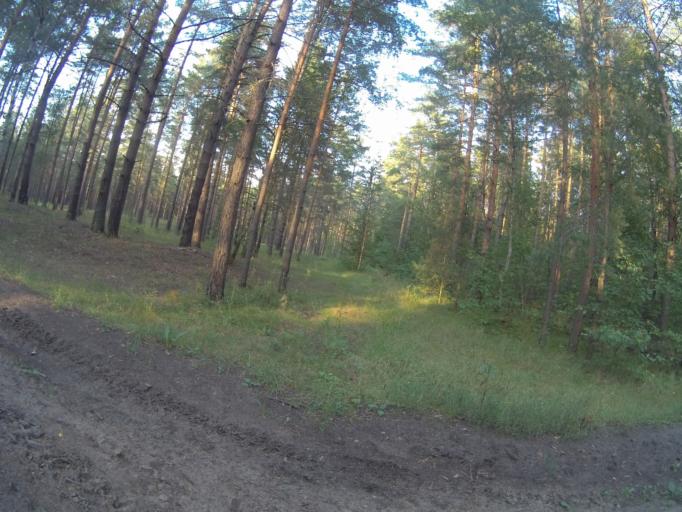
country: RU
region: Vladimir
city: Kommunar
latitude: 56.0801
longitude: 40.4375
